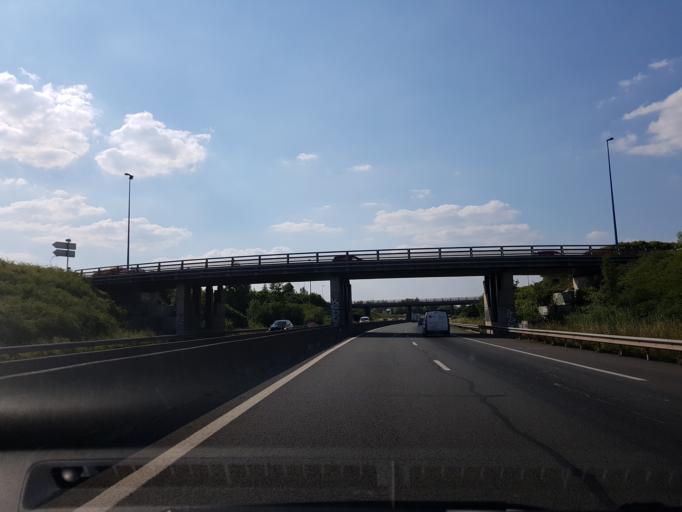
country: FR
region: Nord-Pas-de-Calais
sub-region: Departement du Nord
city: Waziers
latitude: 50.3828
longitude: 3.1341
